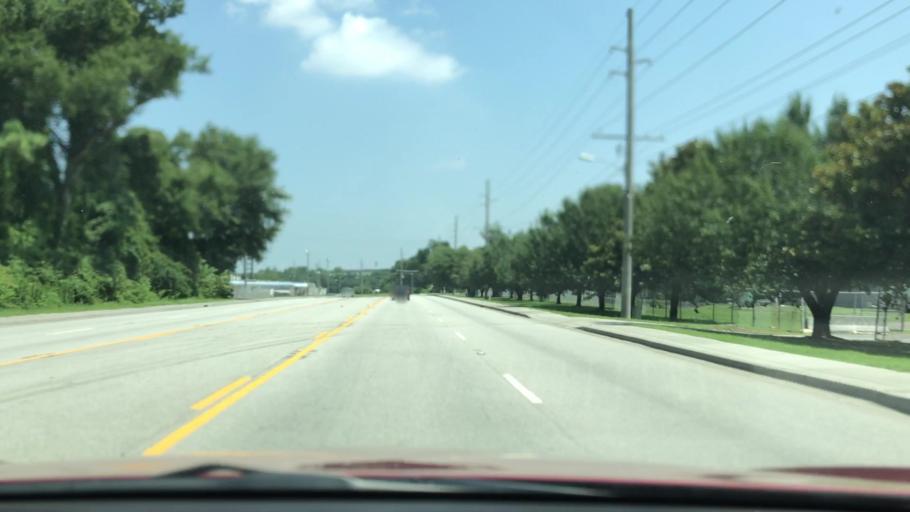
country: US
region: South Carolina
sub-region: Charleston County
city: North Charleston
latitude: 32.8851
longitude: -79.9735
